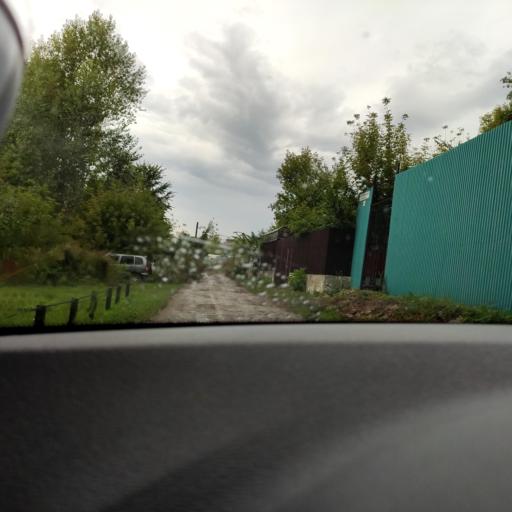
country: RU
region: Samara
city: Samara
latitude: 53.1721
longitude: 50.1586
